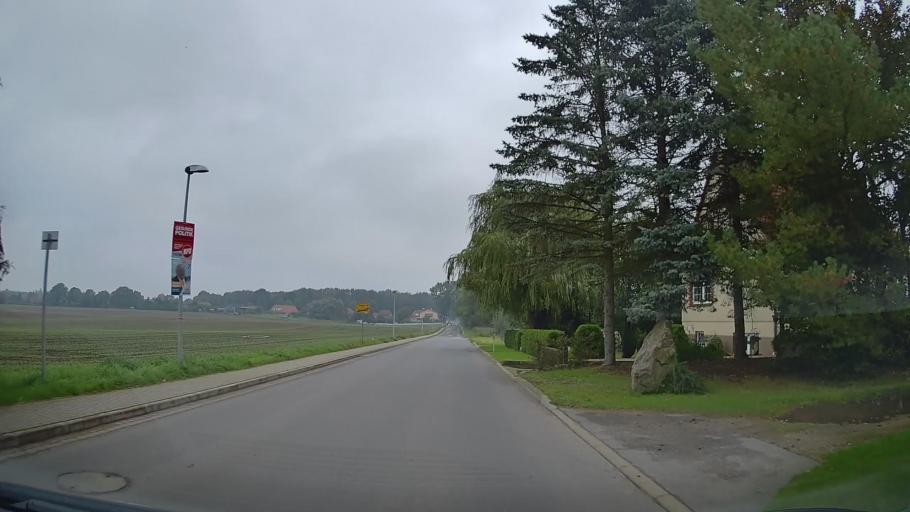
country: DE
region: Mecklenburg-Vorpommern
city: Hornstorf
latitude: 53.9130
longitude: 11.5318
